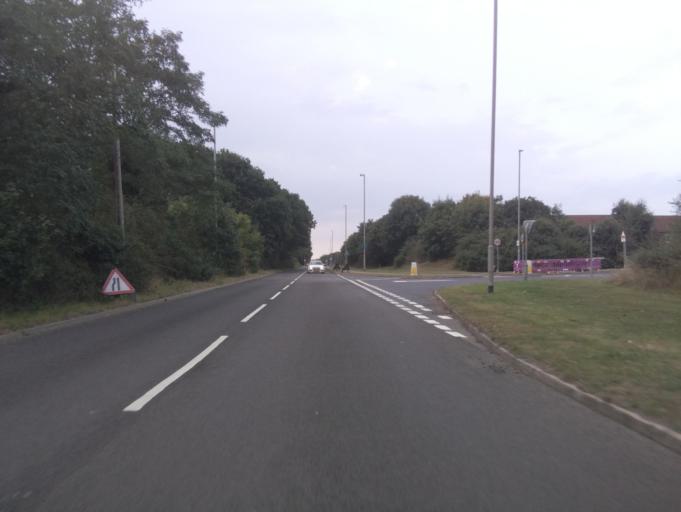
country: GB
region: England
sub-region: Nottinghamshire
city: South Collingham
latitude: 53.1458
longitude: -0.6688
